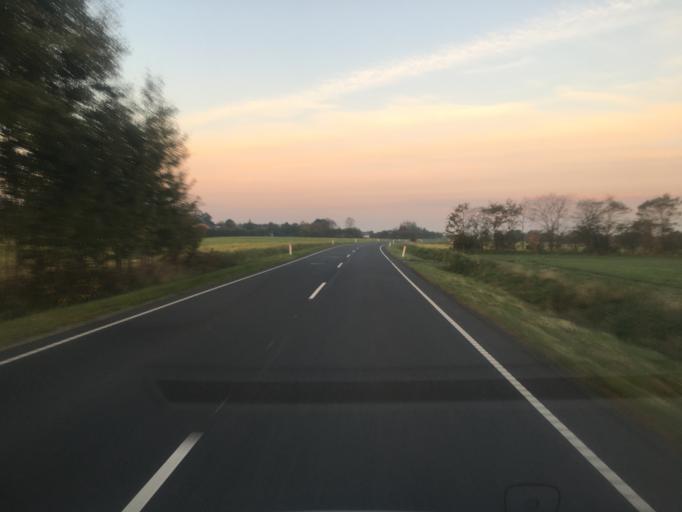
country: DE
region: Schleswig-Holstein
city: Bramstedtlund
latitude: 54.9715
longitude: 9.0879
